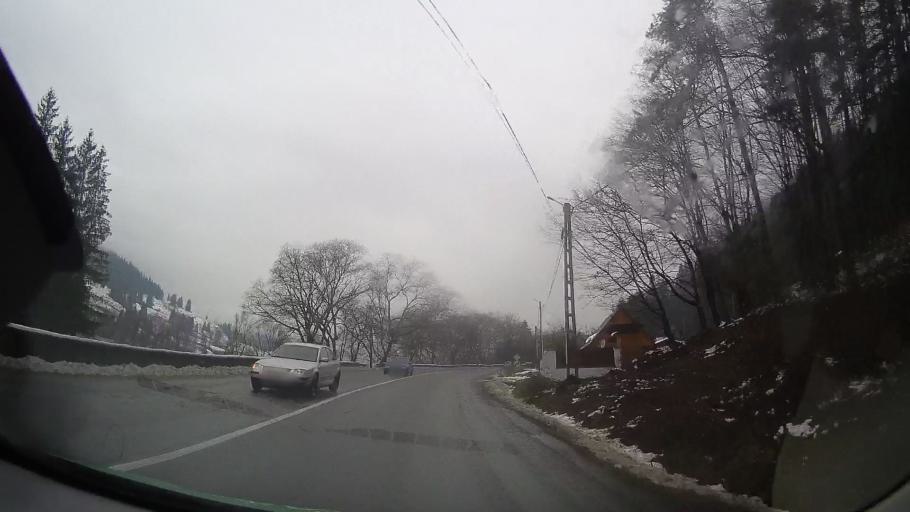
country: RO
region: Neamt
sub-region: Comuna Tarcau
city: Tarcau
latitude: 46.8921
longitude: 26.1242
